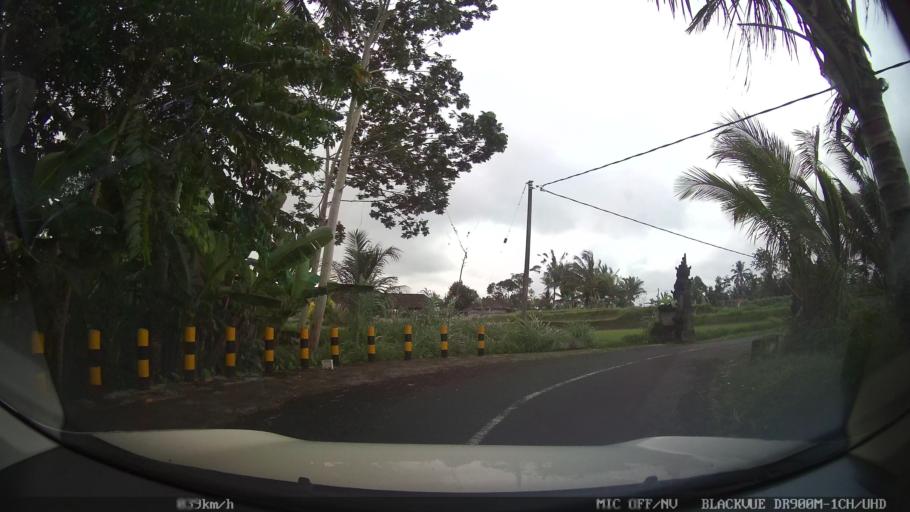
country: ID
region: Bali
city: Badung
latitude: -8.4231
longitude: 115.2271
